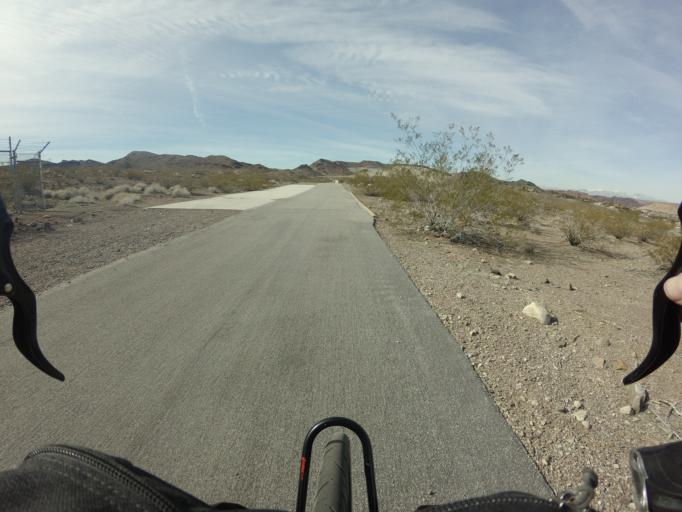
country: US
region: Nevada
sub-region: Clark County
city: Henderson
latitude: 36.1017
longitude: -114.8982
